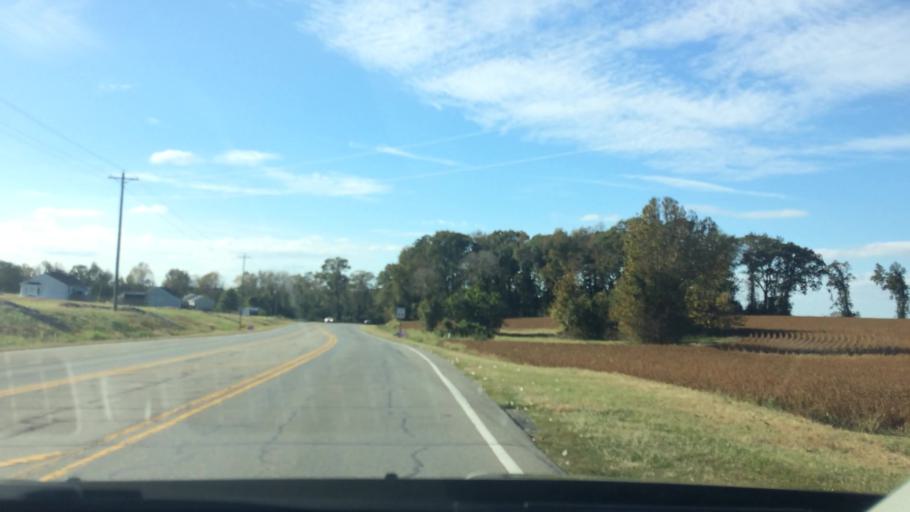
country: US
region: North Carolina
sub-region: Greene County
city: Snow Hill
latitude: 35.4561
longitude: -77.6929
